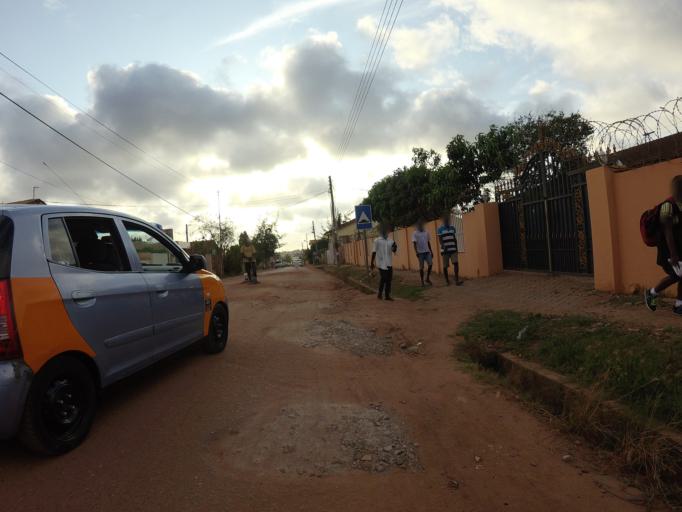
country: GH
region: Greater Accra
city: Nungua
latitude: 5.6190
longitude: -0.0982
